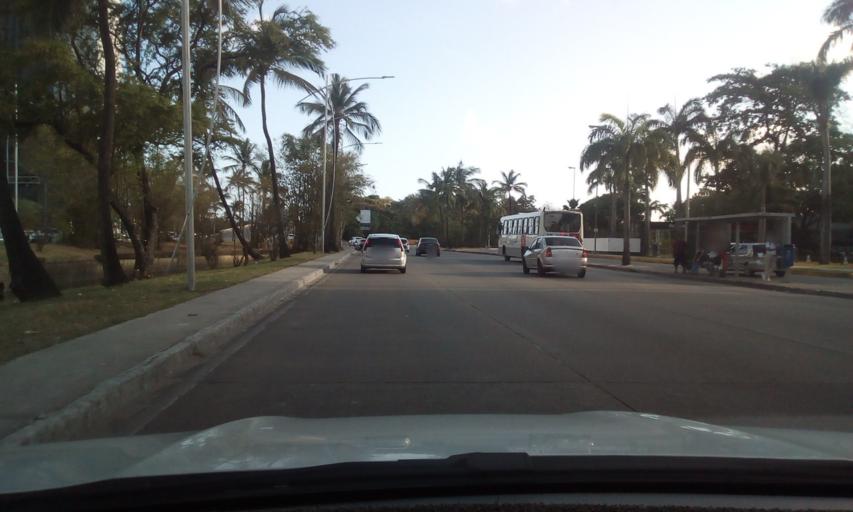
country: BR
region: Pernambuco
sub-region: Recife
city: Recife
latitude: -8.0640
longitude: -34.8975
